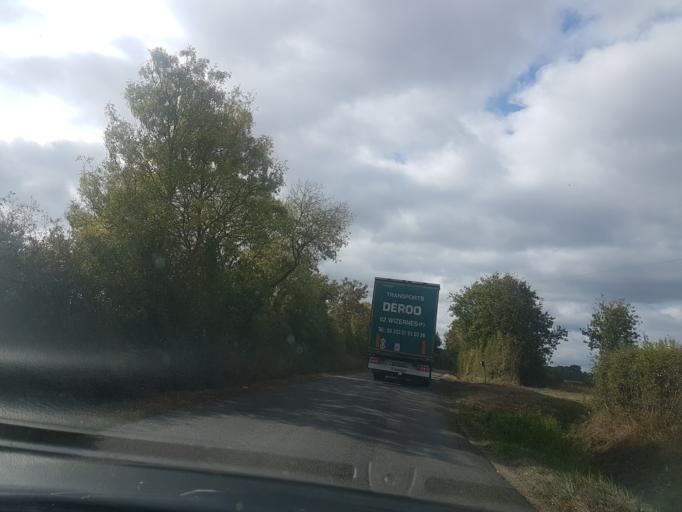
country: FR
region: Pays de la Loire
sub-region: Departement de la Loire-Atlantique
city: Saint-Mars-du-Desert
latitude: 47.3957
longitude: -1.4060
